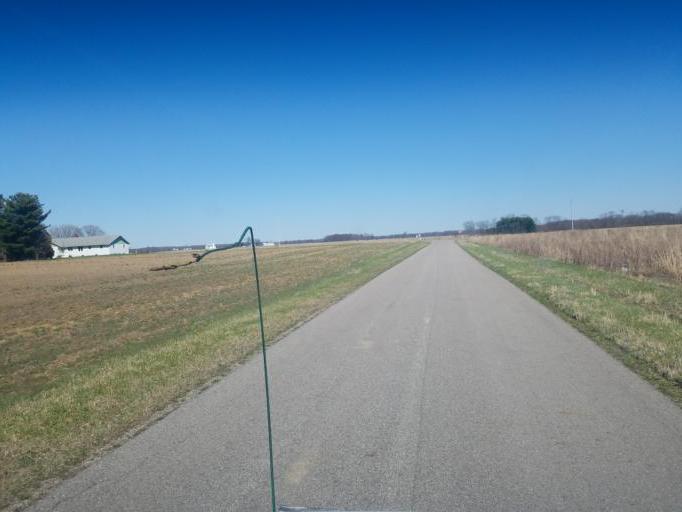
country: US
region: Ohio
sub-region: Morrow County
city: Cardington
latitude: 40.5684
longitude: -82.9021
